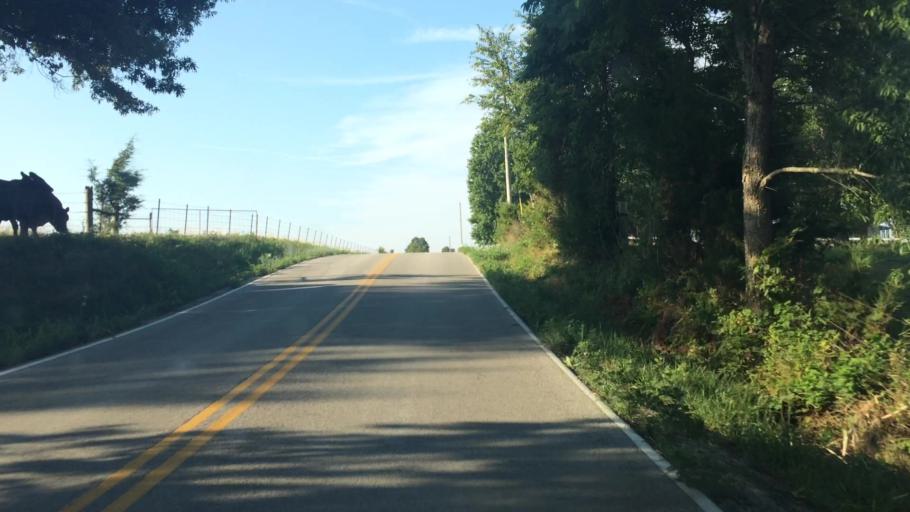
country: US
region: Missouri
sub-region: Greene County
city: Strafford
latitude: 37.2702
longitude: -93.1876
